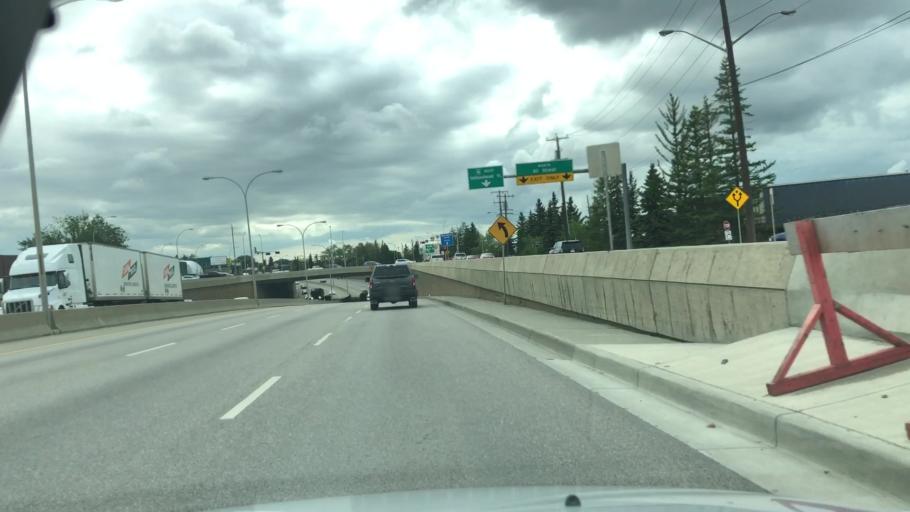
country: CA
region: Alberta
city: Edmonton
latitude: 53.5824
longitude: -113.4643
